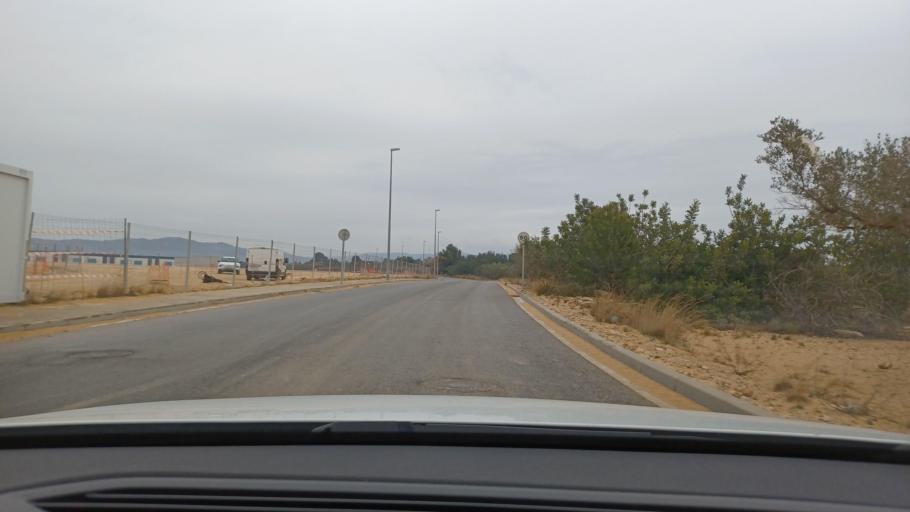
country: ES
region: Catalonia
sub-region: Provincia de Tarragona
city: Amposta
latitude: 40.7636
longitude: 0.5989
